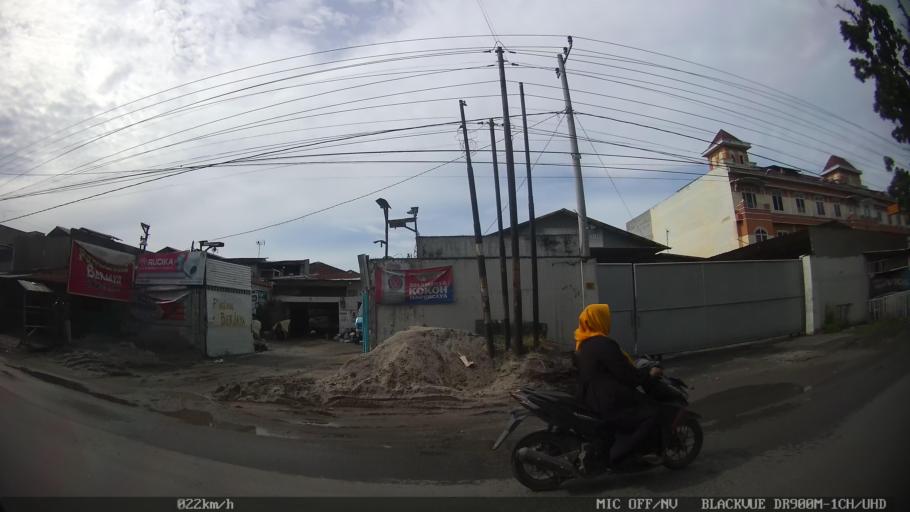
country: ID
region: North Sumatra
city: Medan
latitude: 3.6290
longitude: 98.6972
